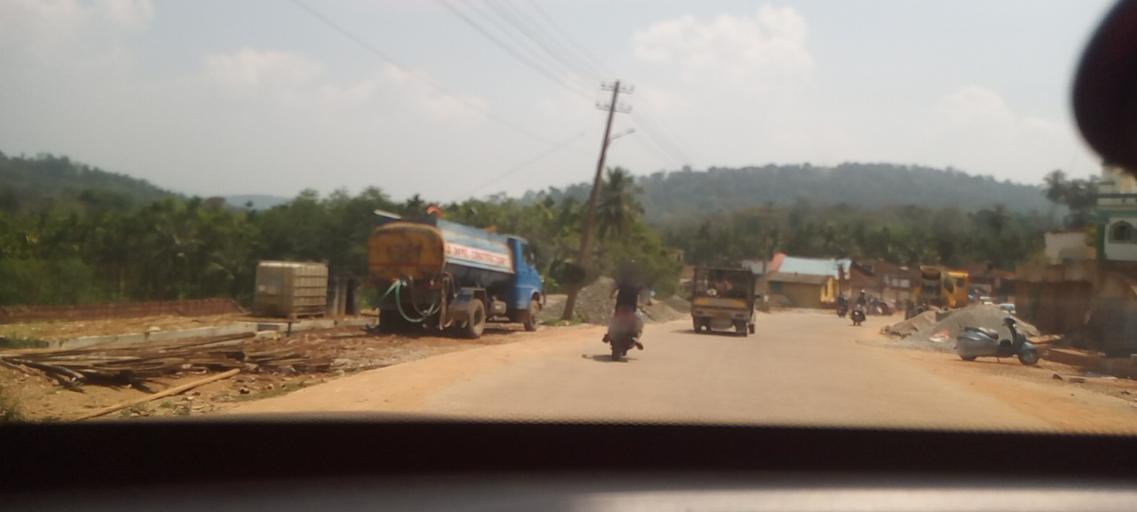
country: IN
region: Karnataka
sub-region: Chikmagalur
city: Koppa
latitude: 13.3510
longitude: 75.4674
